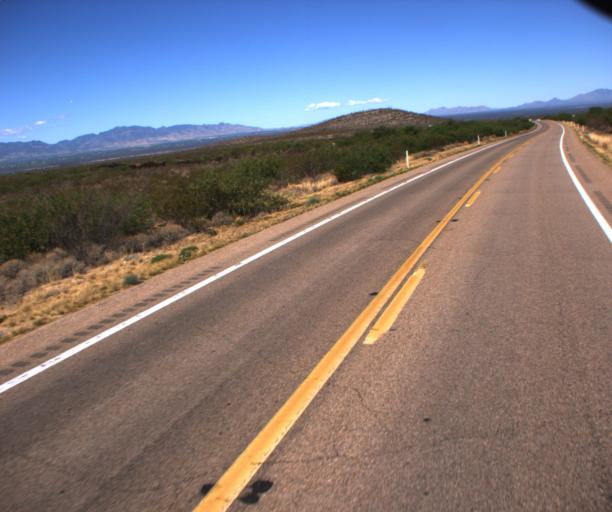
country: US
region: Arizona
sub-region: Cochise County
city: Bisbee
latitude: 31.5231
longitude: -110.0421
